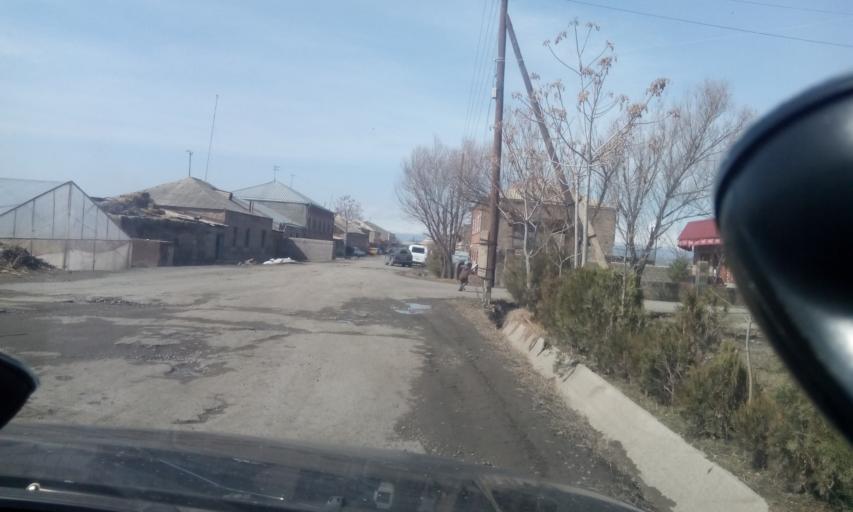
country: AM
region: Armavir
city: Metsamor
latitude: 40.0714
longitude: 44.2889
